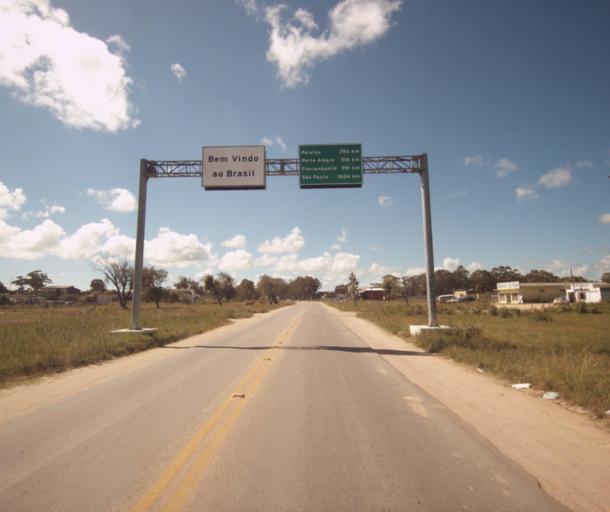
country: BR
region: Rio Grande do Sul
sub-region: Chui
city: Chui
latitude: -33.6924
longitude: -53.4472
